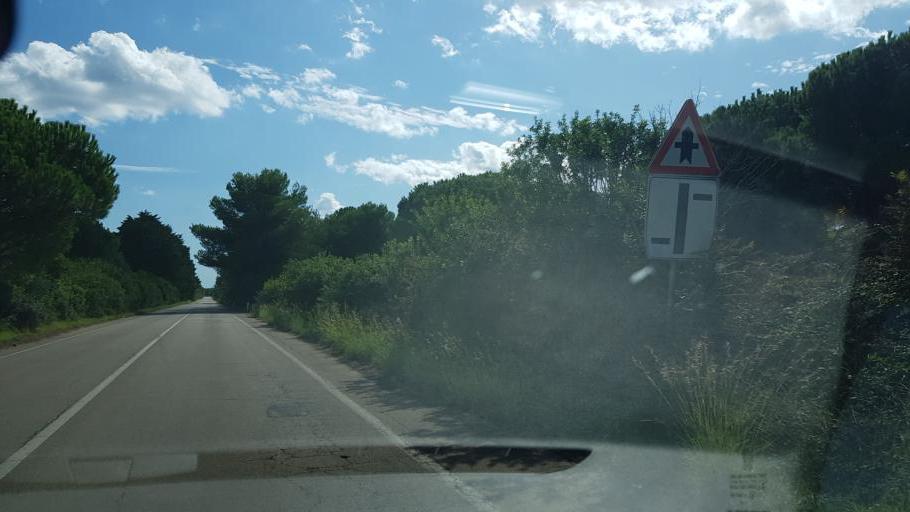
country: IT
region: Apulia
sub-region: Provincia di Lecce
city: Borgagne
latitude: 40.2489
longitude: 18.4407
